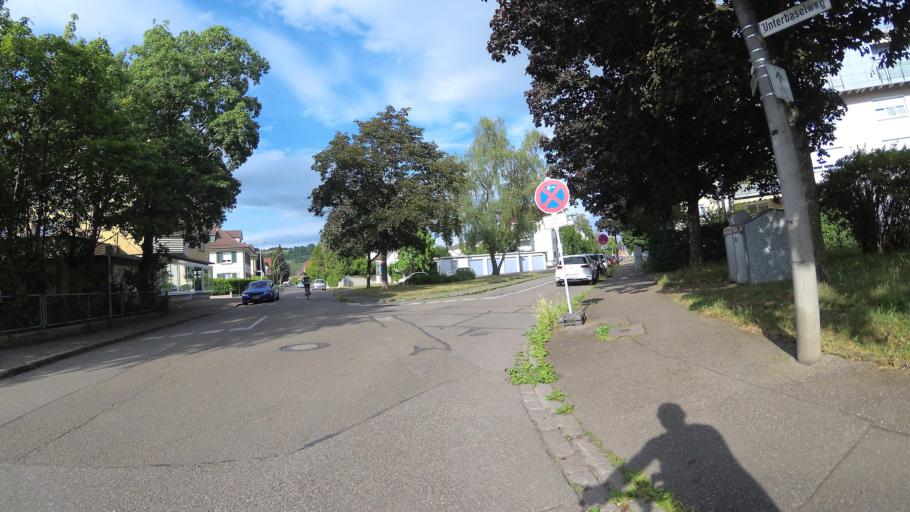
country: DE
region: Baden-Wuerttemberg
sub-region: Freiburg Region
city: Weil am Rhein
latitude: 47.5898
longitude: 7.6232
